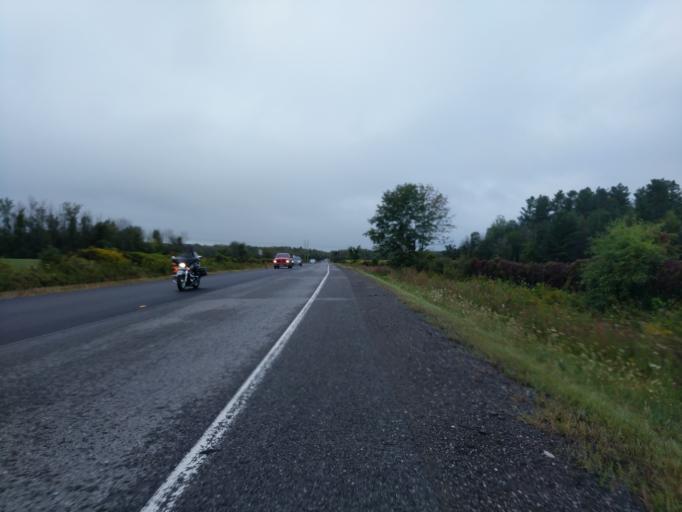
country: CA
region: Ontario
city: Bells Corners
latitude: 45.3252
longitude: -75.8439
